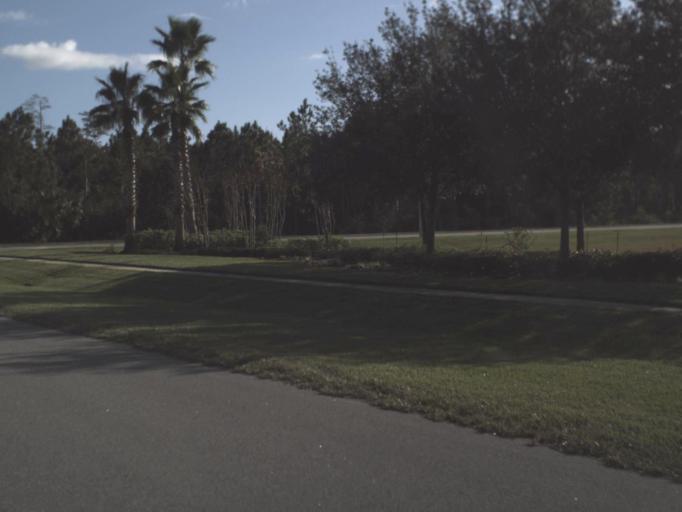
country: US
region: Florida
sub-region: Volusia County
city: Ormond Beach
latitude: 29.2463
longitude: -81.1053
